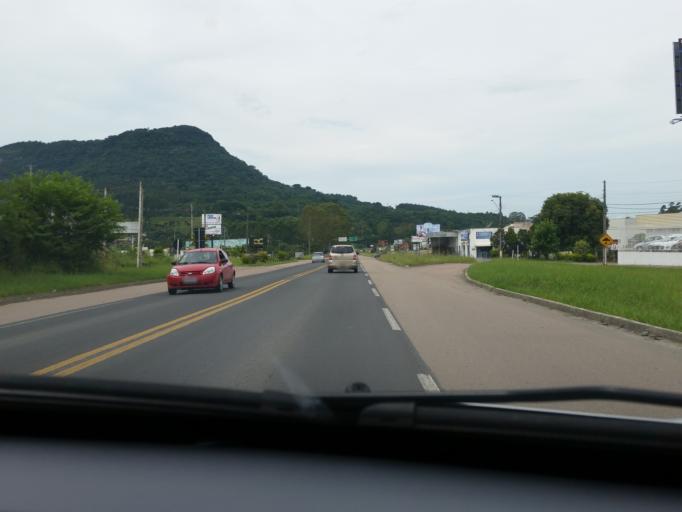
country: BR
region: Santa Catarina
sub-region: Rio Do Sul
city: Rio do Sul
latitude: -27.1947
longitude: -49.6250
